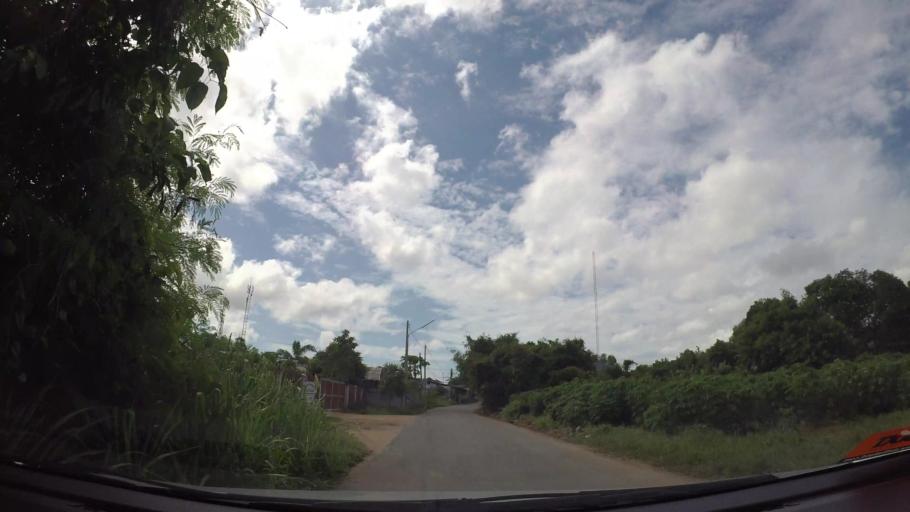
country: TH
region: Chon Buri
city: Sattahip
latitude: 12.6905
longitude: 100.8985
